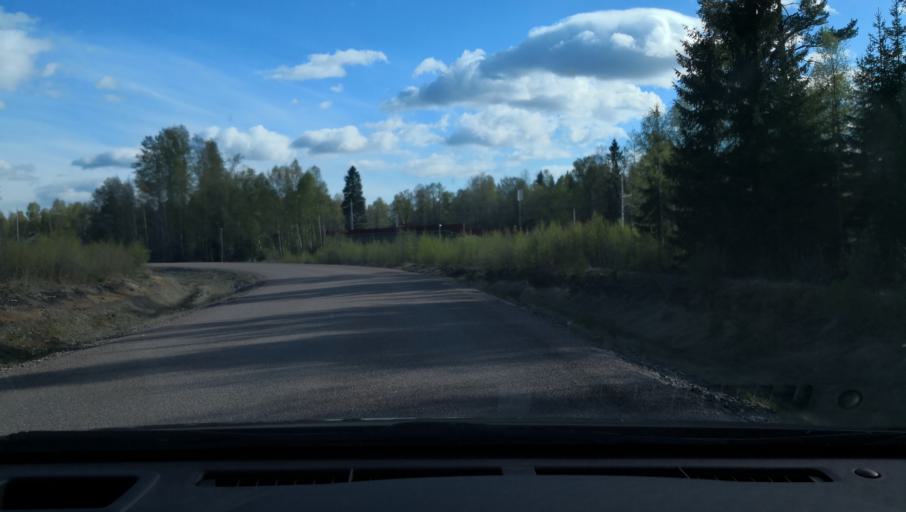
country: SE
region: OErebro
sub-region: Askersunds Kommun
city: Asbro
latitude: 58.9234
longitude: 15.0512
